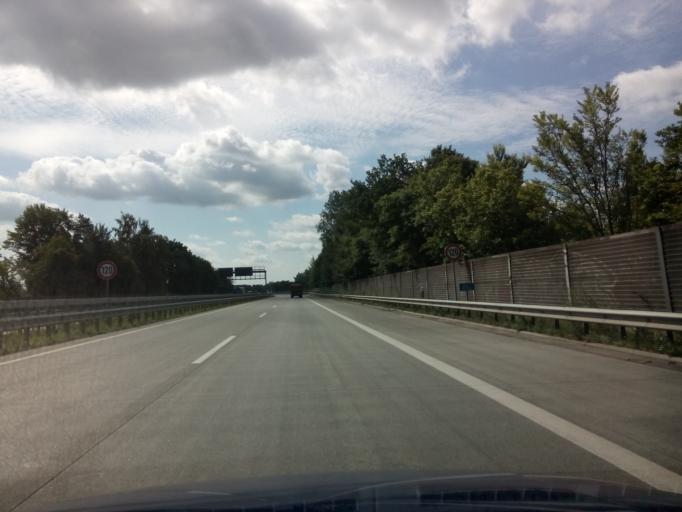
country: DE
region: Lower Saxony
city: Ritterhude
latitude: 53.1861
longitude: 8.7049
